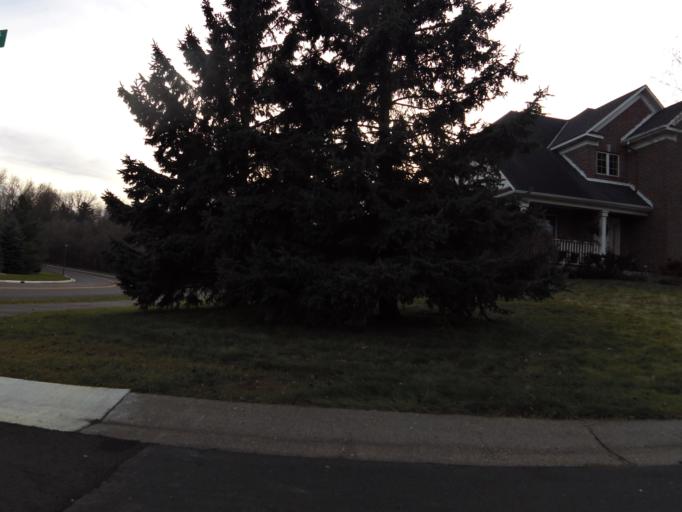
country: US
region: Wisconsin
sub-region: Saint Croix County
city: Hudson
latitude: 44.9716
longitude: -92.7349
